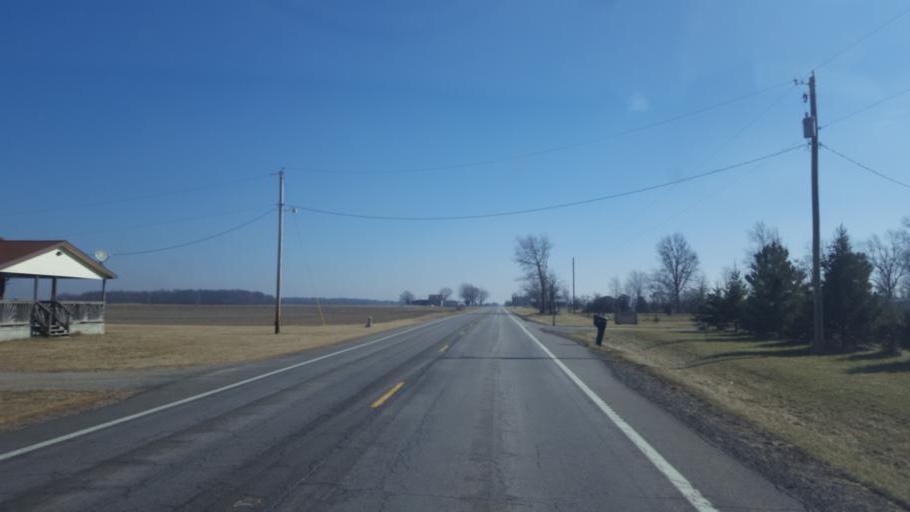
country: US
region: Ohio
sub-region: Huron County
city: Willard
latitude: 41.0442
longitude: -82.7896
